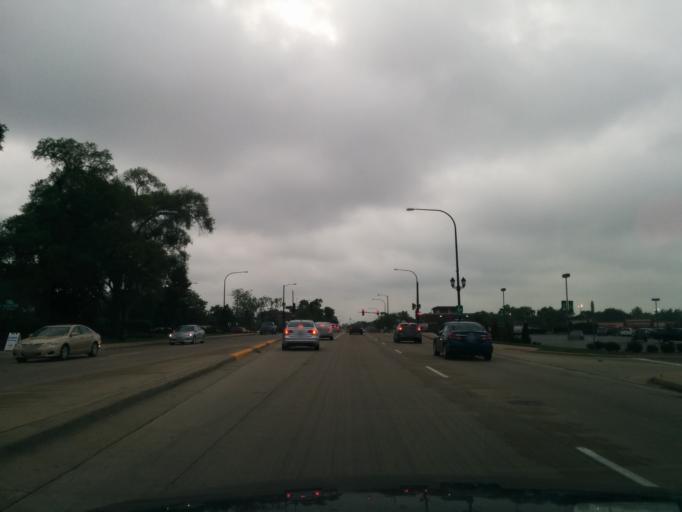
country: US
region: Illinois
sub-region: DuPage County
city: Addison
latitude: 41.9335
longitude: -87.9921
